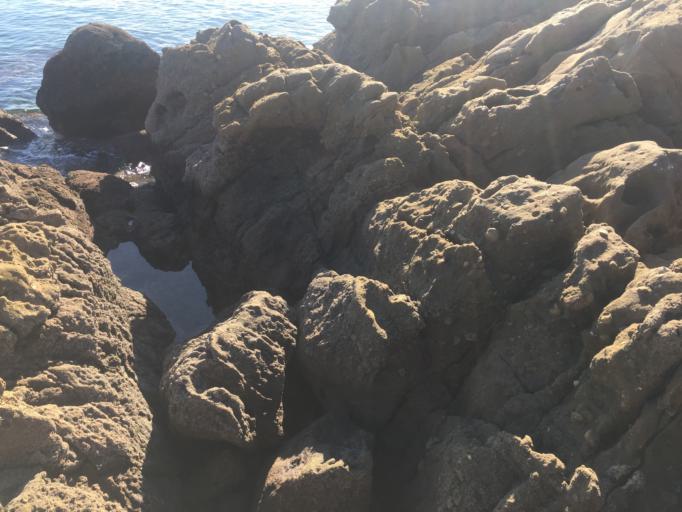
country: JP
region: Nagasaki
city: Nagasaki-shi
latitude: 32.6886
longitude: 129.7924
